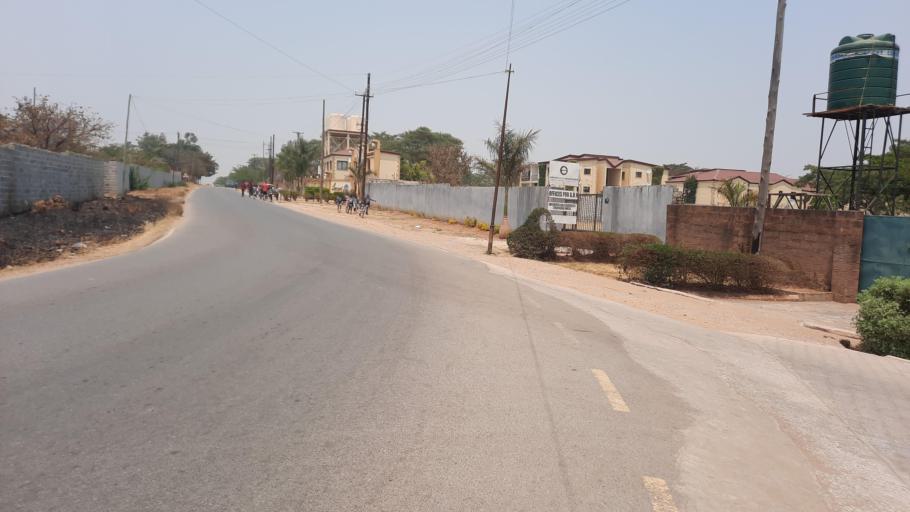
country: ZM
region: Lusaka
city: Lusaka
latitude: -15.4124
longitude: 28.3620
